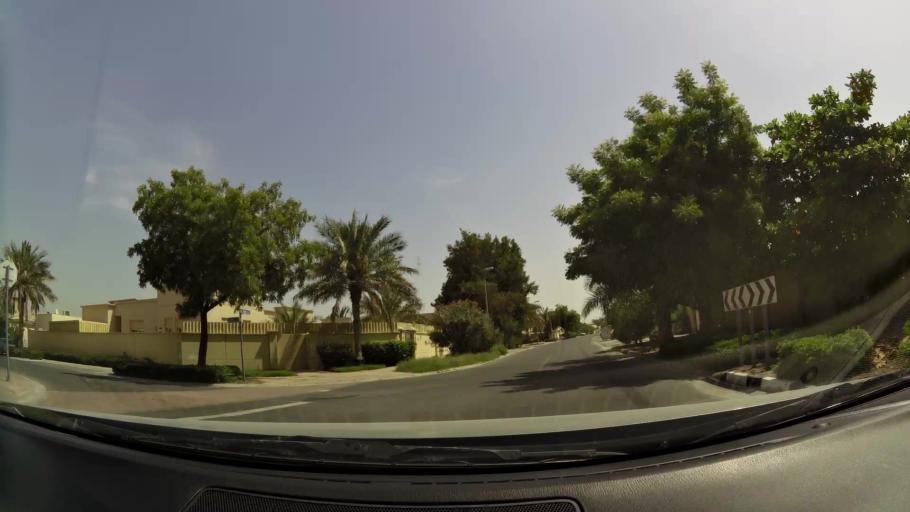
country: AE
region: Ash Shariqah
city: Sharjah
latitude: 25.1794
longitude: 55.4402
